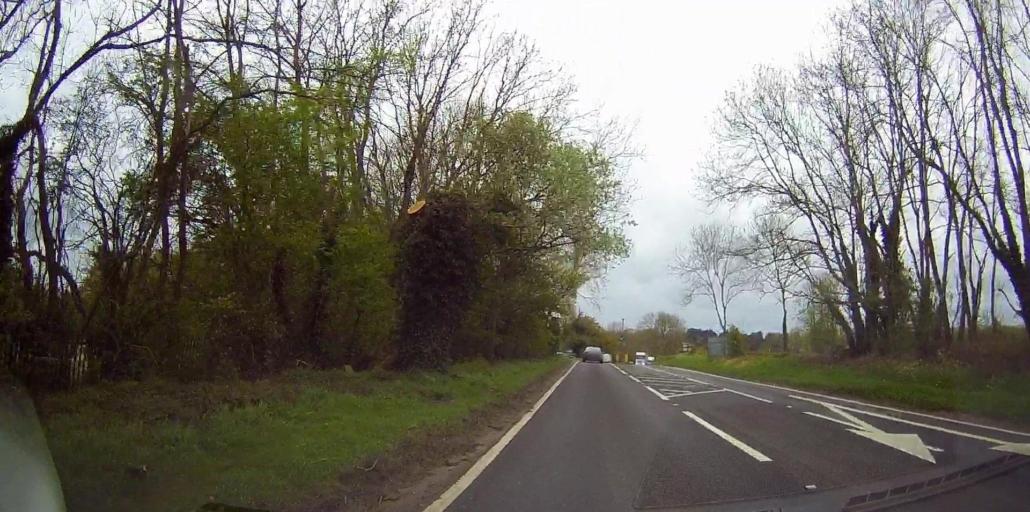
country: GB
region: England
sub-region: Kent
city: Lenham
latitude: 51.2407
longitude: 0.7070
